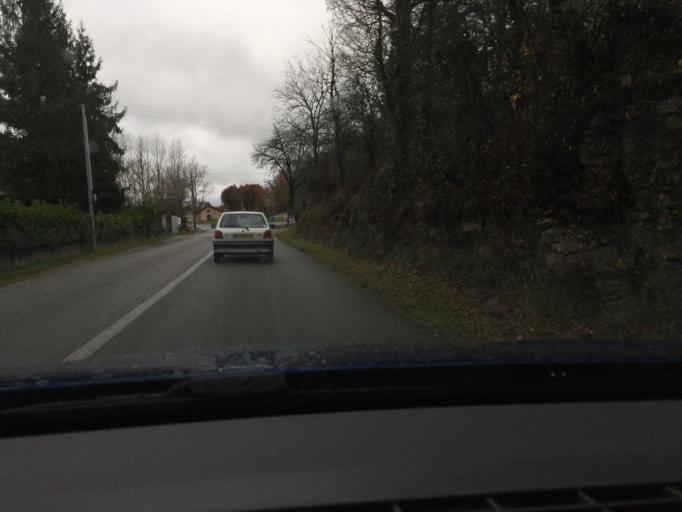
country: FR
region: Midi-Pyrenees
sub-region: Departement de l'Aveyron
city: Villefranche-de-Rouergue
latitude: 44.3762
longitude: 2.0115
